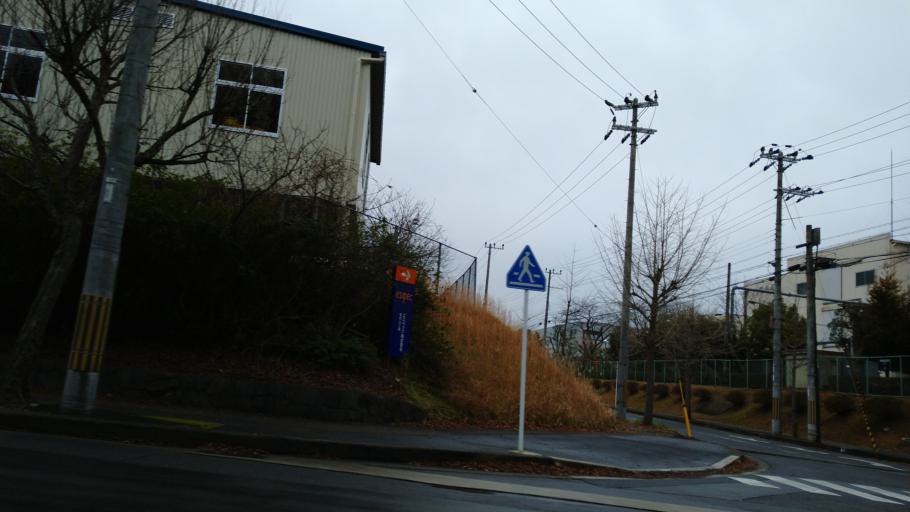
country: JP
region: Kyoto
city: Fukuchiyama
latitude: 35.2905
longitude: 135.1581
